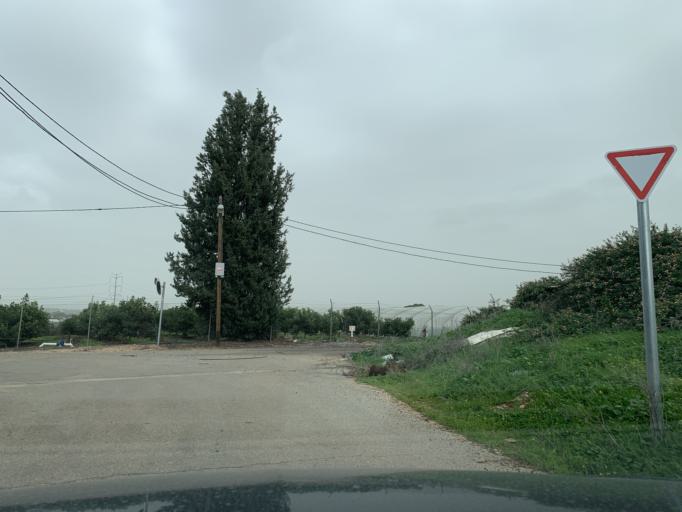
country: IL
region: Central District
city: Jaljulya
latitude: 32.1624
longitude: 34.9461
